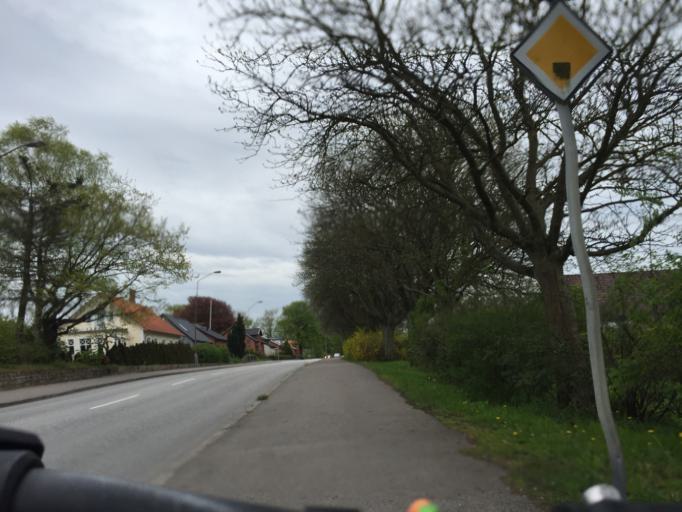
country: SE
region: Skane
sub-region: Lunds Kommun
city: Veberod
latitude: 55.6395
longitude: 13.4856
